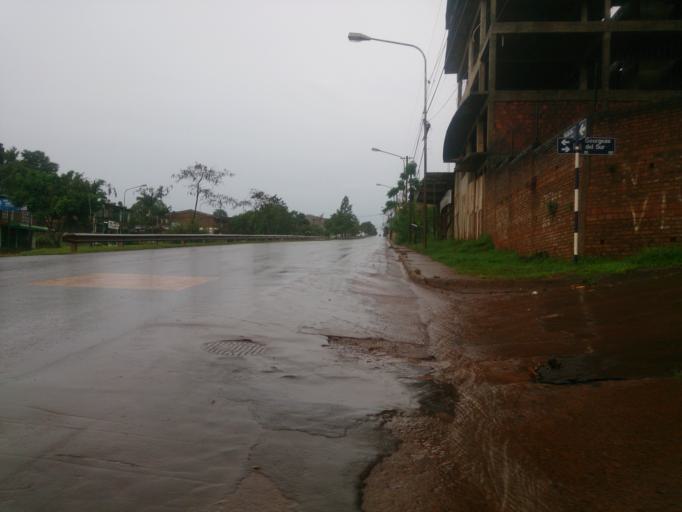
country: AR
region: Misiones
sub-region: Departamento de Obera
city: Obera
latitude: -27.4788
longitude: -55.1040
